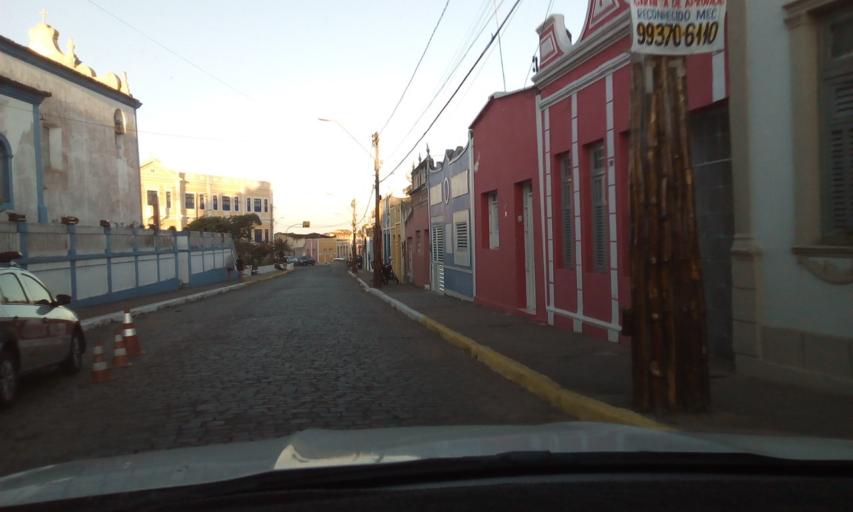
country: BR
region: Paraiba
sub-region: Areia
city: Areia
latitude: -6.9684
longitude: -35.7010
